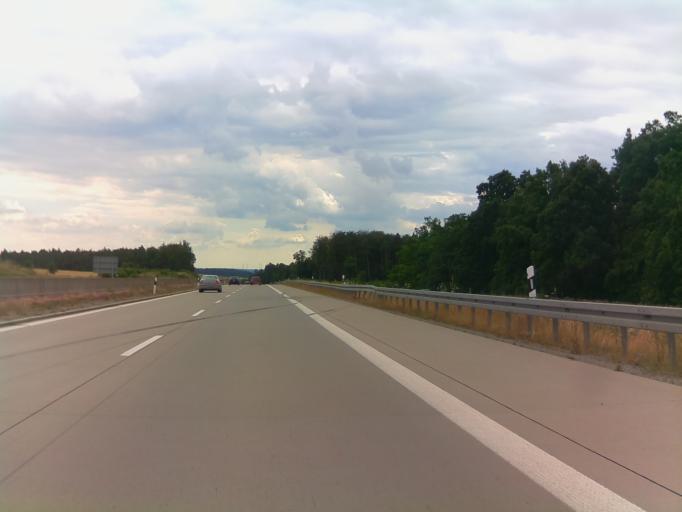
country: DE
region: Bavaria
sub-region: Regierungsbezirk Unterfranken
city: Hendungen
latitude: 50.4052
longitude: 10.3245
